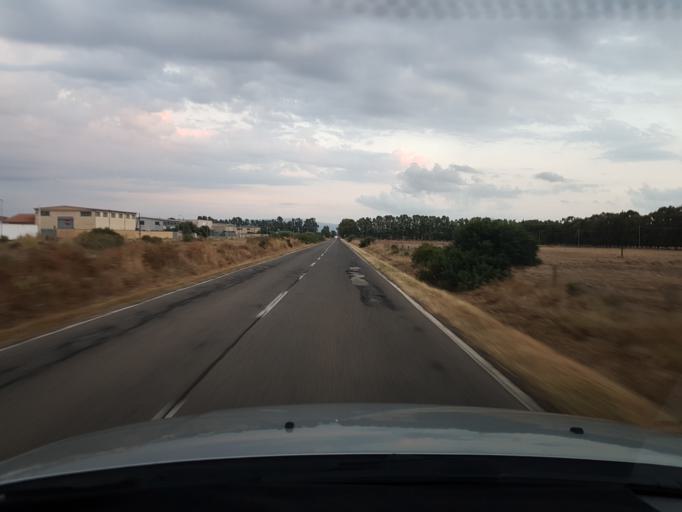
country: IT
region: Sardinia
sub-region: Provincia di Oristano
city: Milis
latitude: 40.0381
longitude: 8.6371
